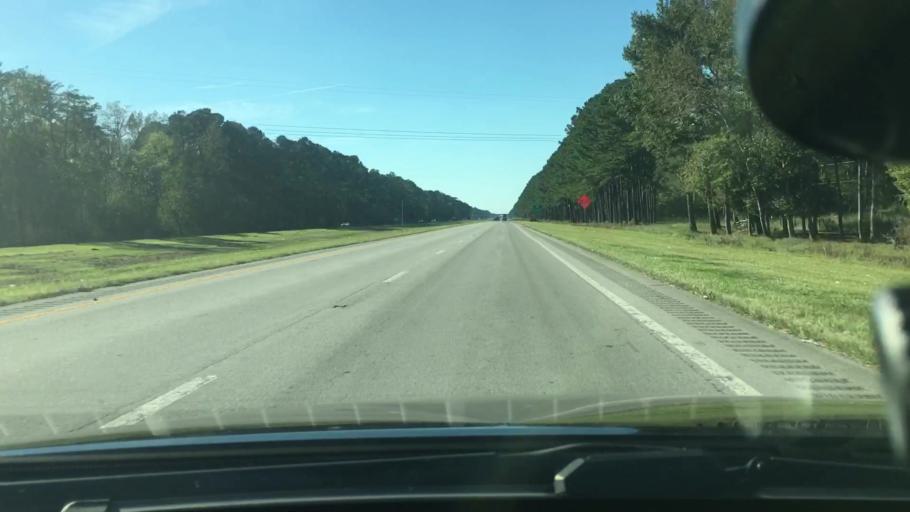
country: US
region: North Carolina
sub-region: Craven County
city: Trent Woods
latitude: 35.1216
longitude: -77.1156
